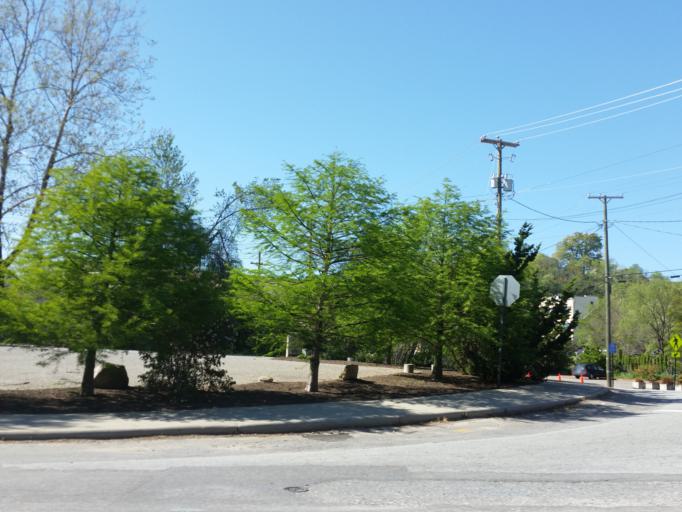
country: US
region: North Carolina
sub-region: Buncombe County
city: Asheville
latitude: 35.5844
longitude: -82.5664
